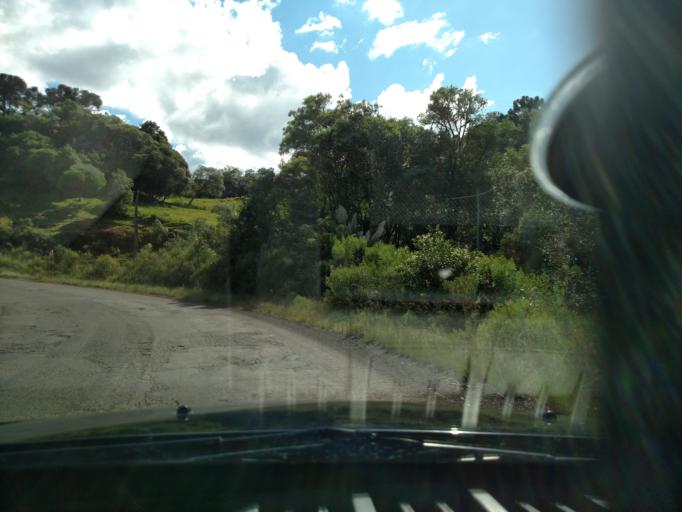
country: BR
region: Santa Catarina
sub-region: Lages
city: Lages
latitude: -27.9198
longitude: -50.6265
